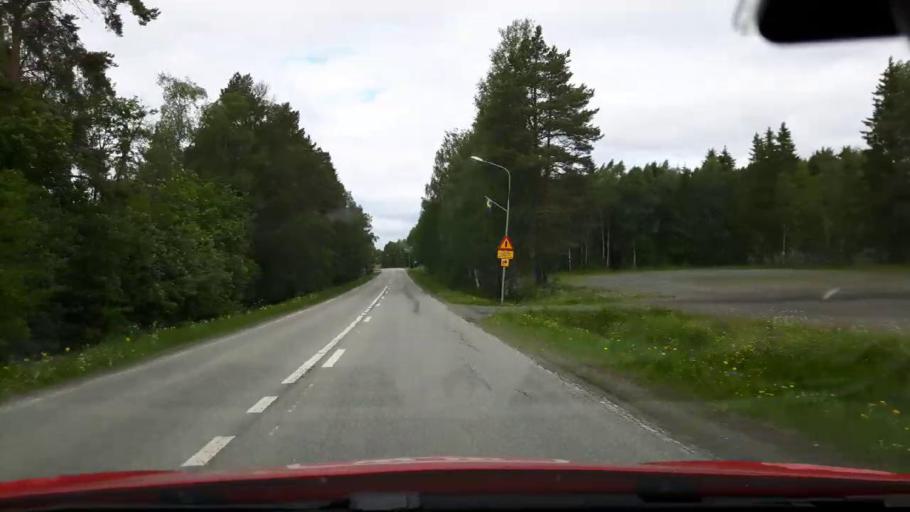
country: SE
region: Jaemtland
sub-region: Krokoms Kommun
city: Krokom
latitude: 63.2973
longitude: 14.4835
